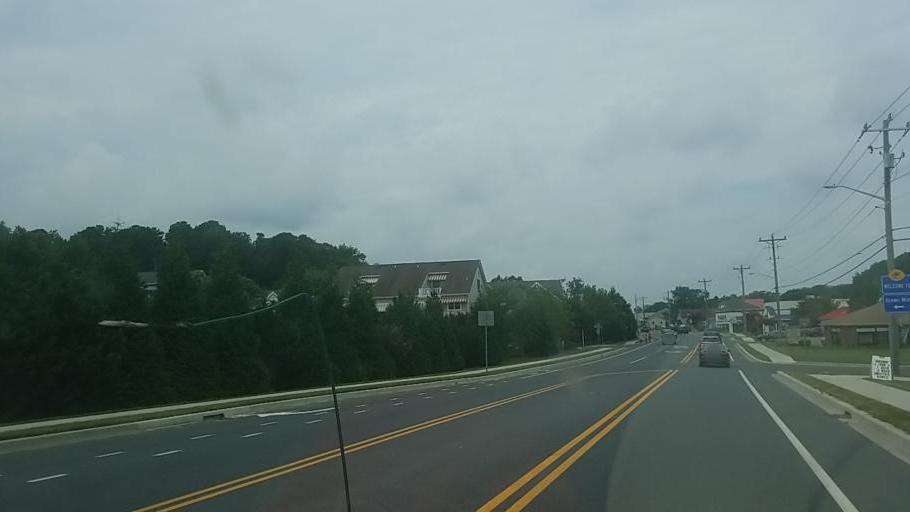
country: US
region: Delaware
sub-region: Sussex County
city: Ocean View
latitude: 38.5428
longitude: -75.0816
